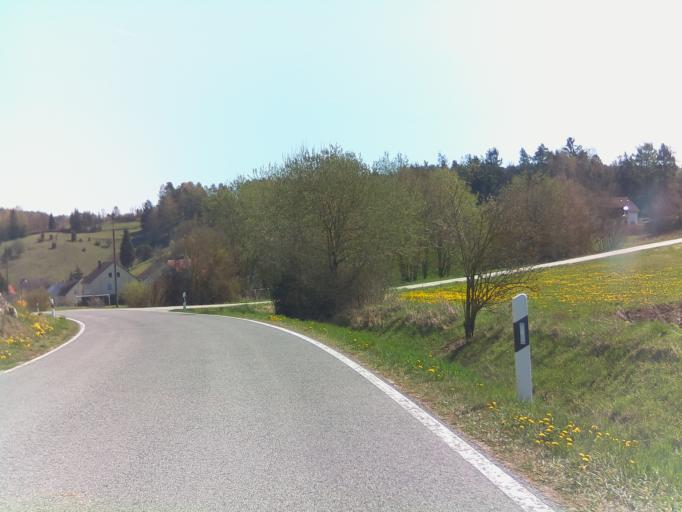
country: DE
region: Bavaria
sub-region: Regierungsbezirk Mittelfranken
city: Alfeld
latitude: 49.4277
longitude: 11.5369
